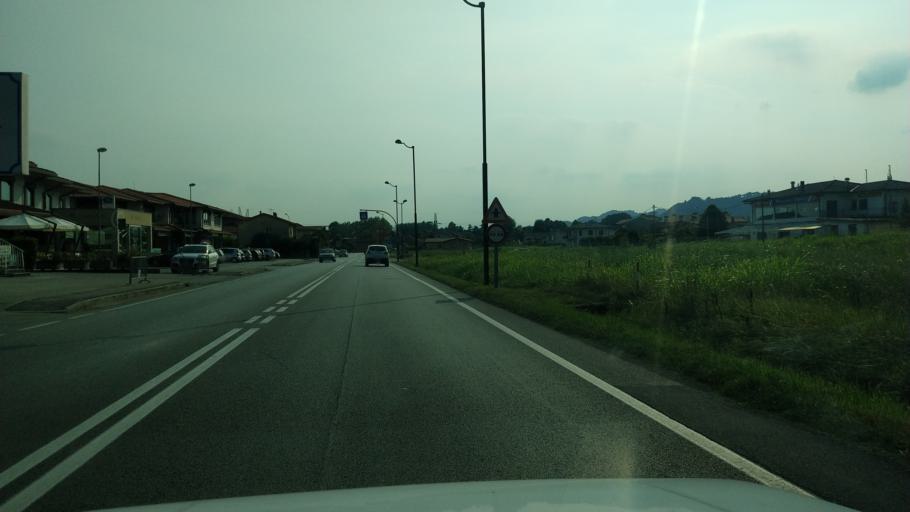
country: IT
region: Veneto
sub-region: Provincia di Vicenza
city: Bassano del Grappa
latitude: 45.7605
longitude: 11.7084
